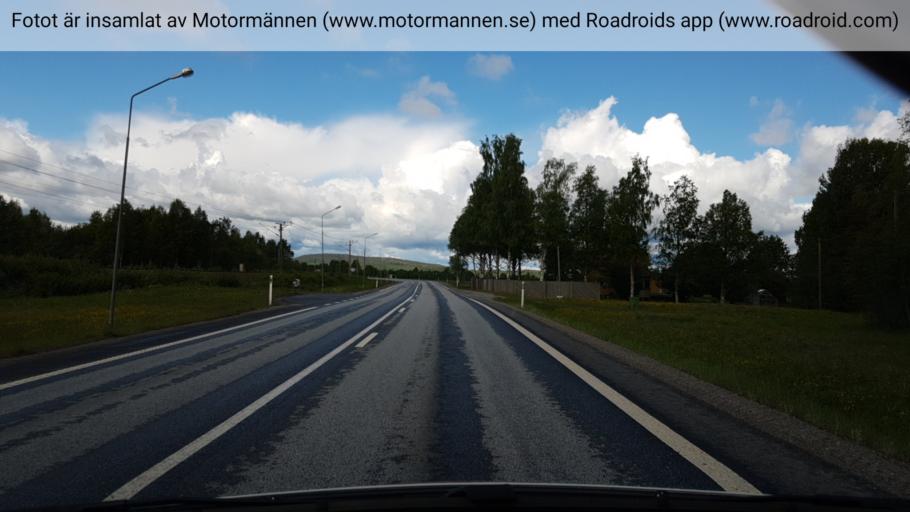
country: SE
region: Vaesterbotten
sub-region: Vannas Kommun
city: Vannasby
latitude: 63.9193
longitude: 19.8722
